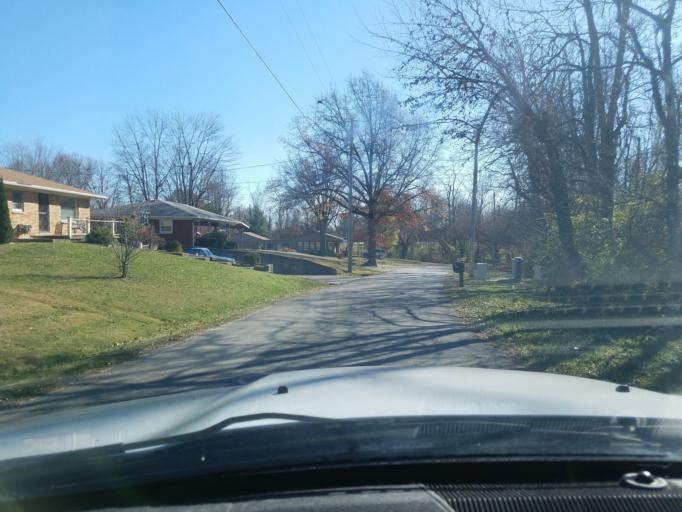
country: US
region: Indiana
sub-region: Floyd County
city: New Albany
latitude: 38.3410
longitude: -85.8116
